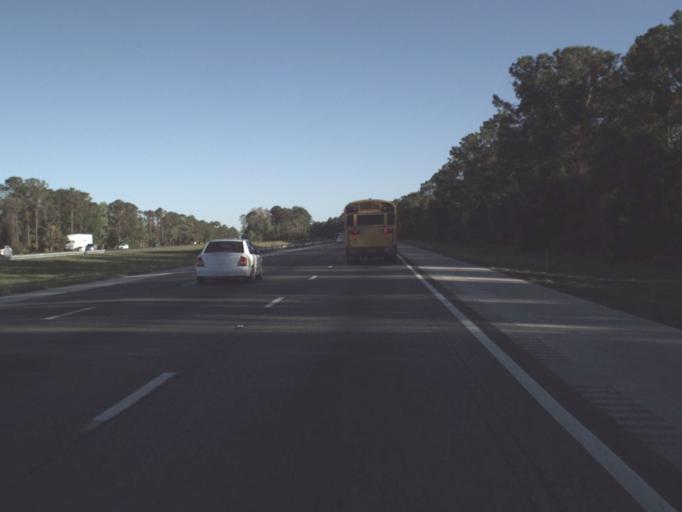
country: US
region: Florida
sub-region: Flagler County
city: Flagler Beach
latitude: 29.4363
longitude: -81.1690
